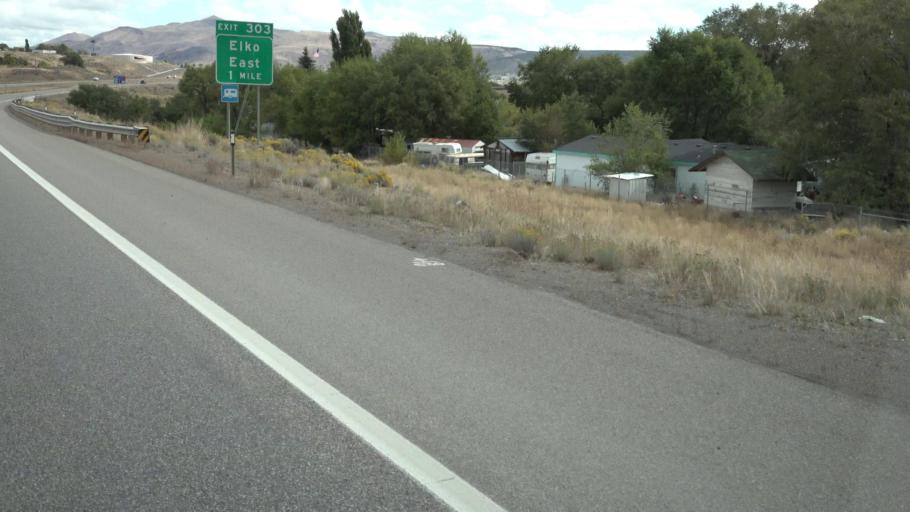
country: US
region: Nevada
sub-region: Elko County
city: Elko
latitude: 40.8428
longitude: -115.7728
